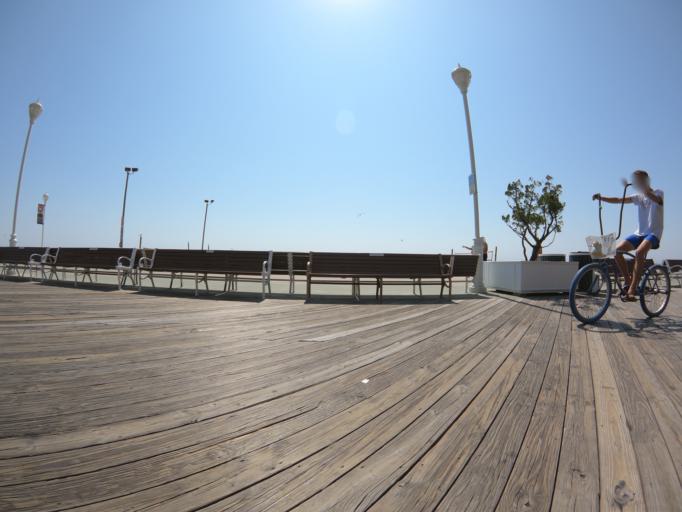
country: US
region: Maryland
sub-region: Worcester County
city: Ocean City
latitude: 38.3347
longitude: -75.0832
